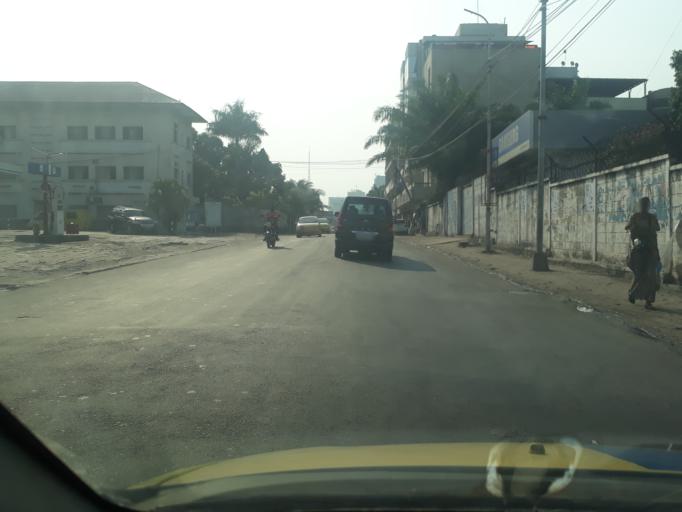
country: CD
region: Kinshasa
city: Kinshasa
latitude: -4.3065
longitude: 15.3242
